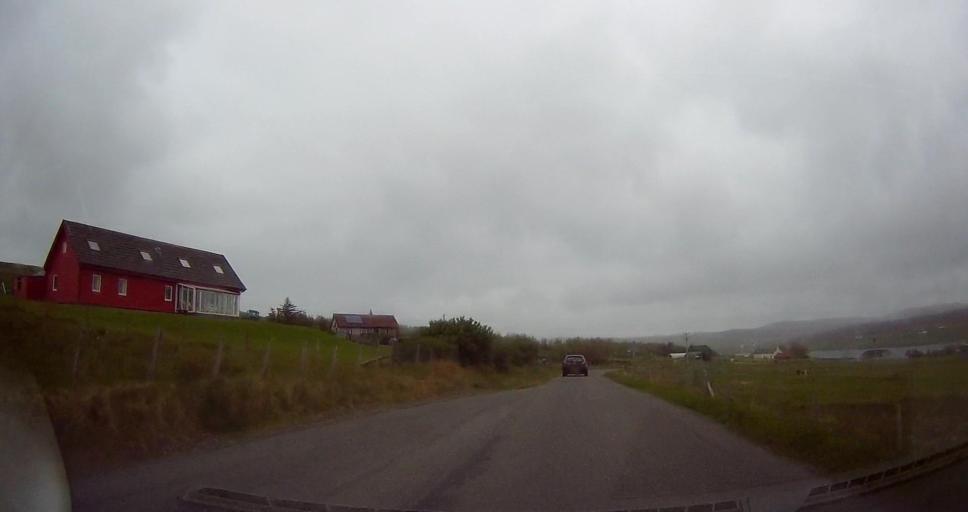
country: GB
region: Scotland
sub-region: Shetland Islands
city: Lerwick
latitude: 60.2835
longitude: -1.3876
